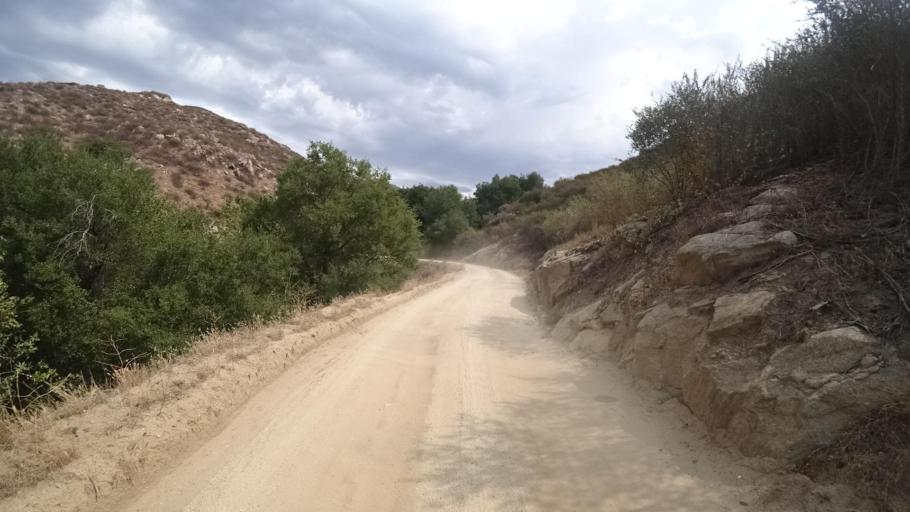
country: US
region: California
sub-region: San Diego County
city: Ramona
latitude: 33.1048
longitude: -116.8225
